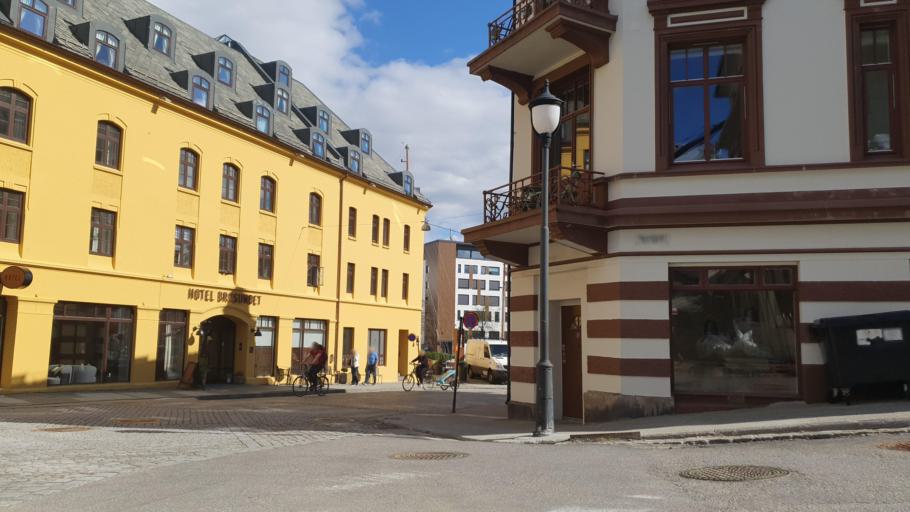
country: NO
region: More og Romsdal
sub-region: Alesund
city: Alesund
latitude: 62.4725
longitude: 6.1519
